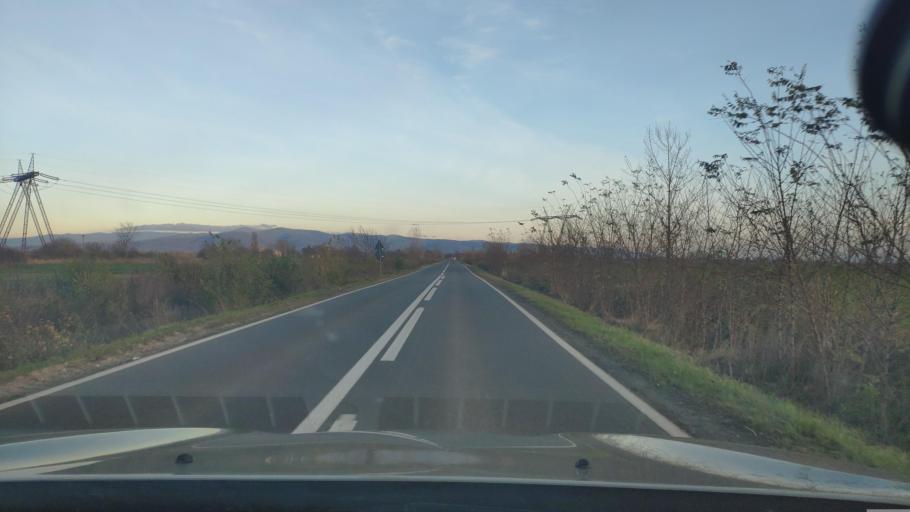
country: RO
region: Satu Mare
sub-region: Comuna Mediesu Aurit
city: Mediesu Aurit
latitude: 47.7674
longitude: 23.1721
